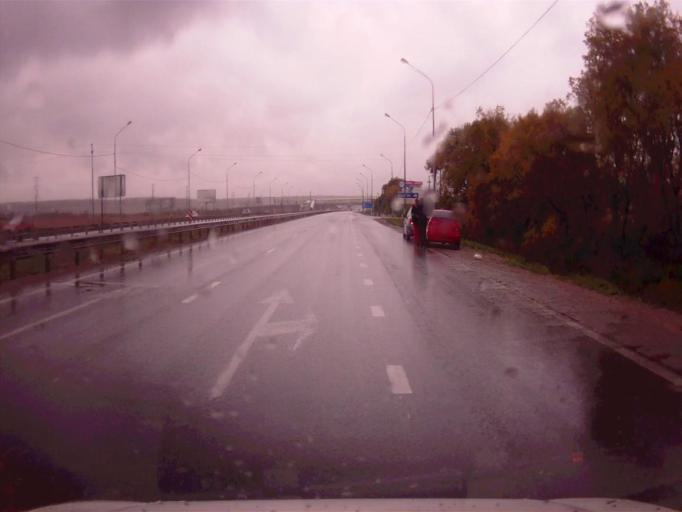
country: RU
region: Chelyabinsk
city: Dolgoderevenskoye
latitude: 55.3073
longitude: 61.3356
